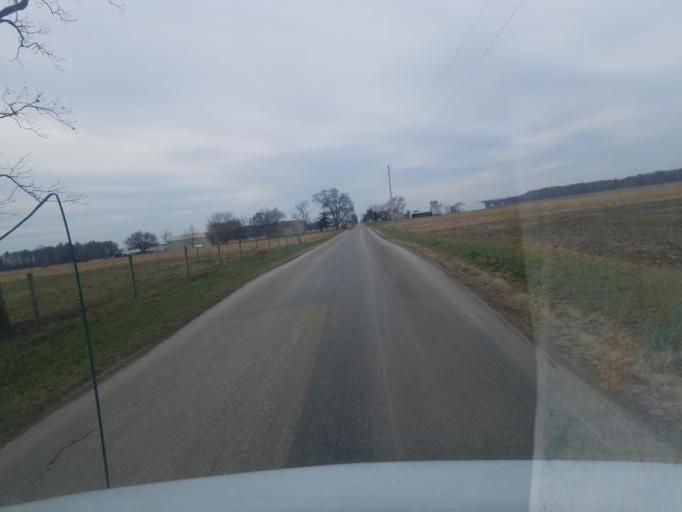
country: US
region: Indiana
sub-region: Adams County
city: Geneva
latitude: 40.6151
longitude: -84.8727
